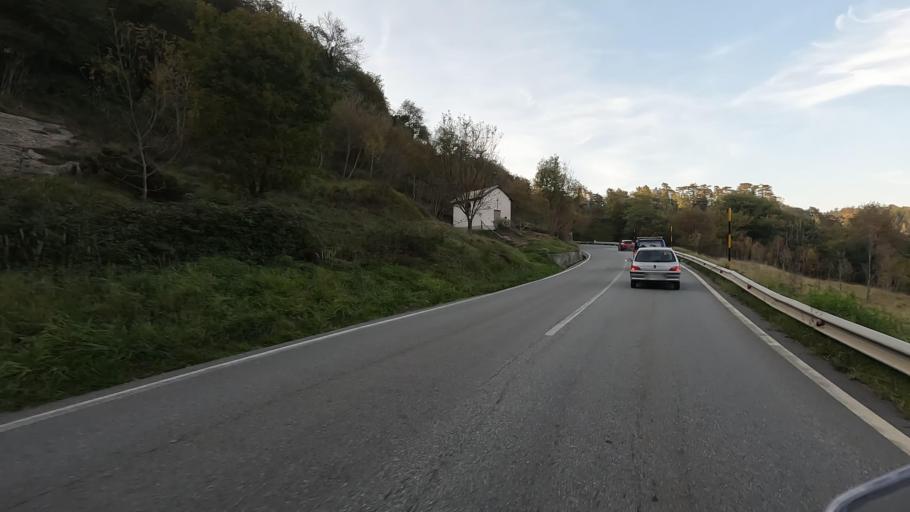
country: IT
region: Liguria
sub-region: Provincia di Savona
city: Osteria dei Cacciatori-Stella
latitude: 44.4258
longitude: 8.4742
